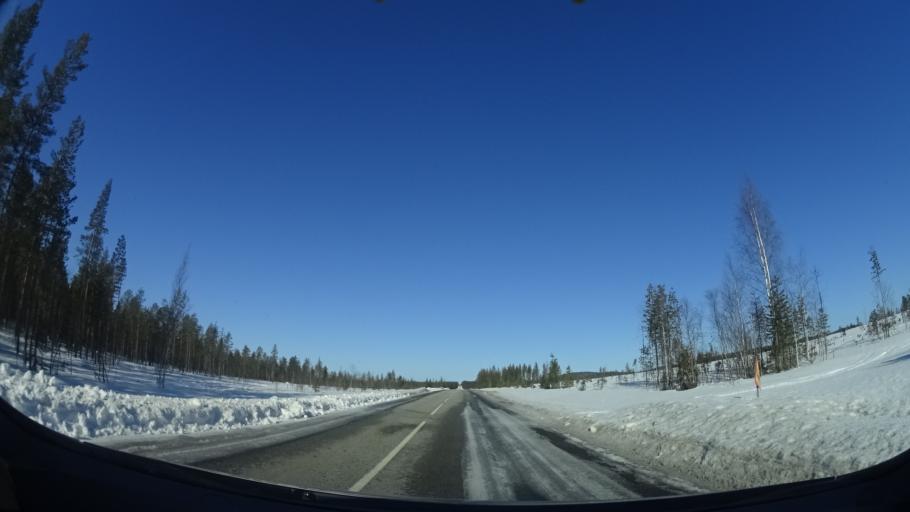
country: SE
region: Vaesterbotten
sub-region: Skelleftea Kommun
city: Langsele
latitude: 65.1029
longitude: 20.0841
